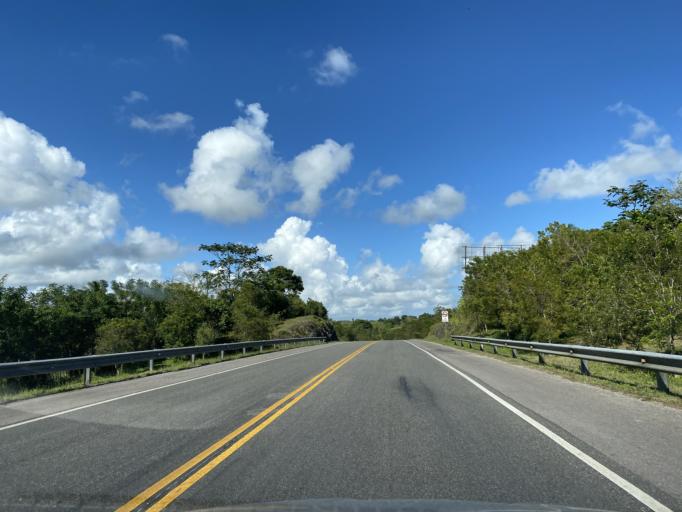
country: DO
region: Monte Plata
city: Majagual
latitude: 19.0213
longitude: -69.8226
